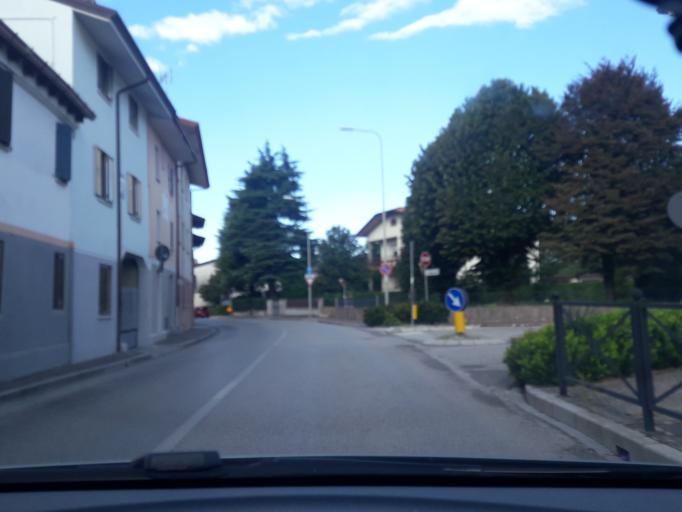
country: IT
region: Friuli Venezia Giulia
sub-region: Provincia di Udine
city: Pasian di Prato
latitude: 46.0497
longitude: 13.1900
